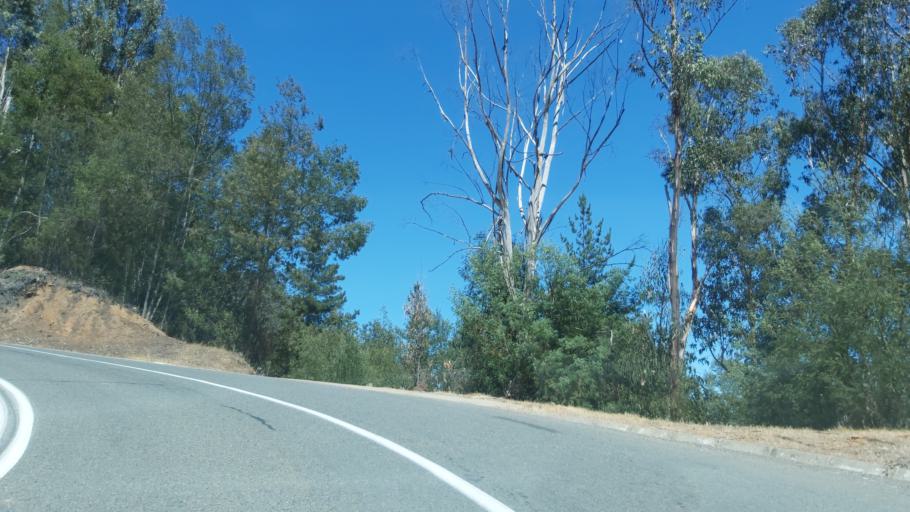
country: CL
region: Maule
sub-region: Provincia de Talca
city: Constitucion
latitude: -34.9091
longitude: -71.9966
